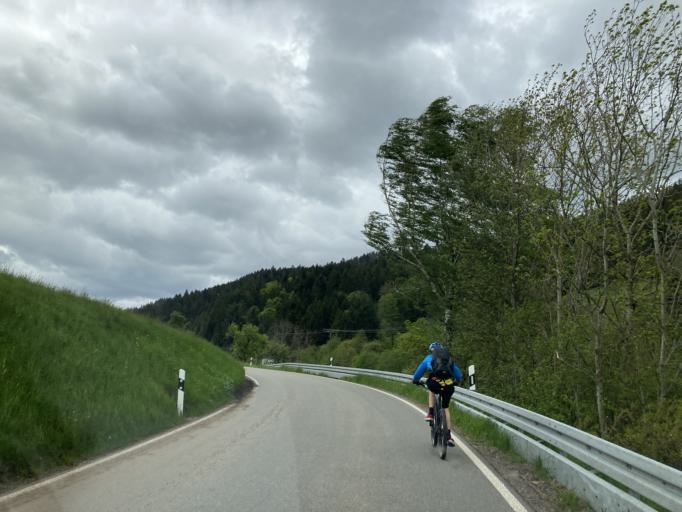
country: DE
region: Baden-Wuerttemberg
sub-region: Freiburg Region
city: Schonach im Schwarzwald
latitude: 48.1901
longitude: 8.1599
